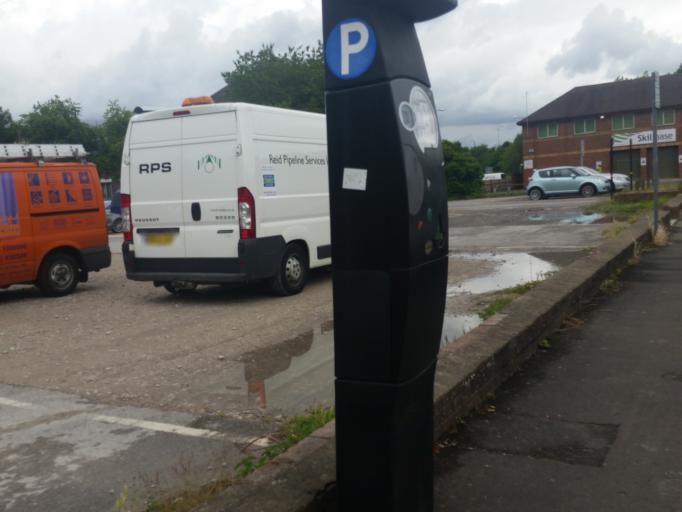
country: GB
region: England
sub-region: Derby
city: Derby
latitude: 52.9201
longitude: -1.4696
